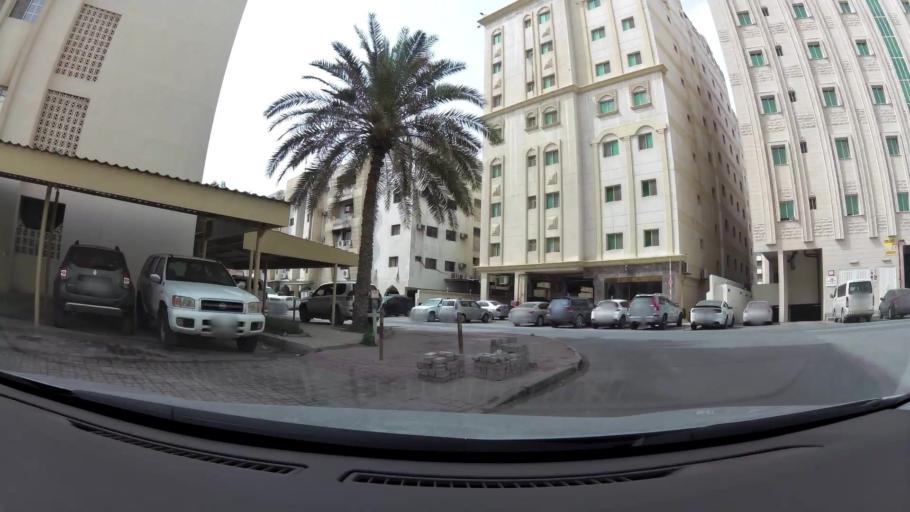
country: QA
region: Baladiyat ad Dawhah
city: Doha
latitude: 25.2668
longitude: 51.5425
